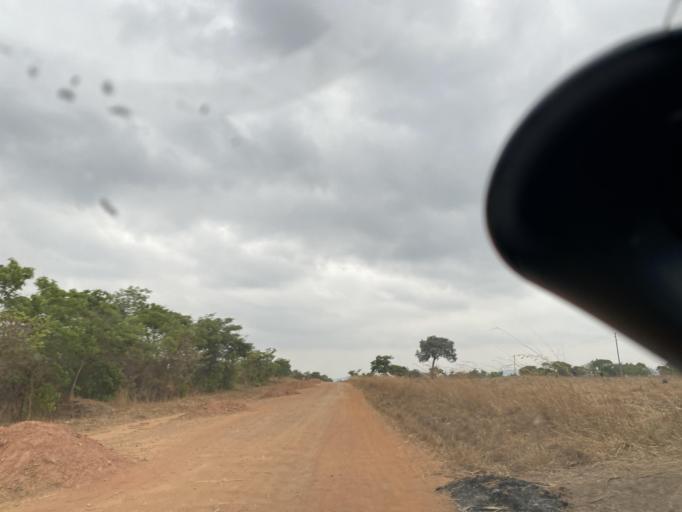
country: ZM
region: Lusaka
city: Chongwe
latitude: -15.2585
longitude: 28.7309
